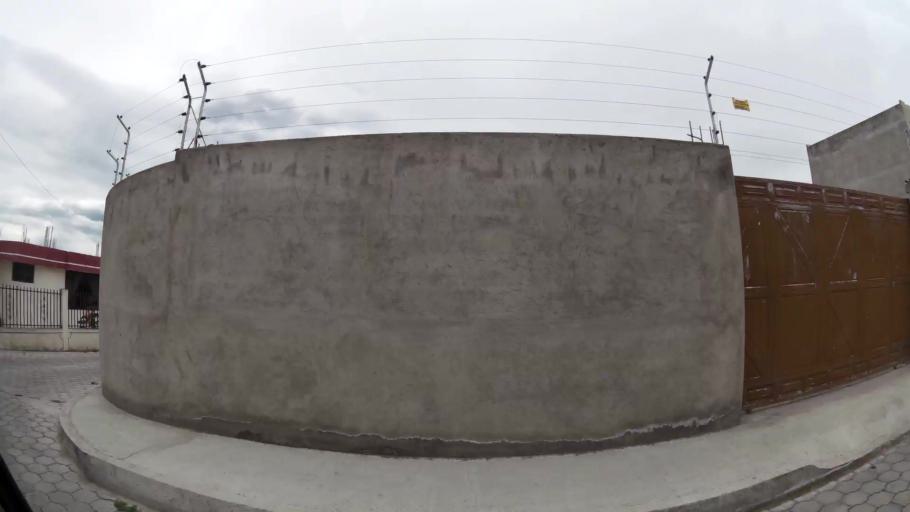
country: EC
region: Cotopaxi
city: Latacunga
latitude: -0.9478
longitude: -78.6095
